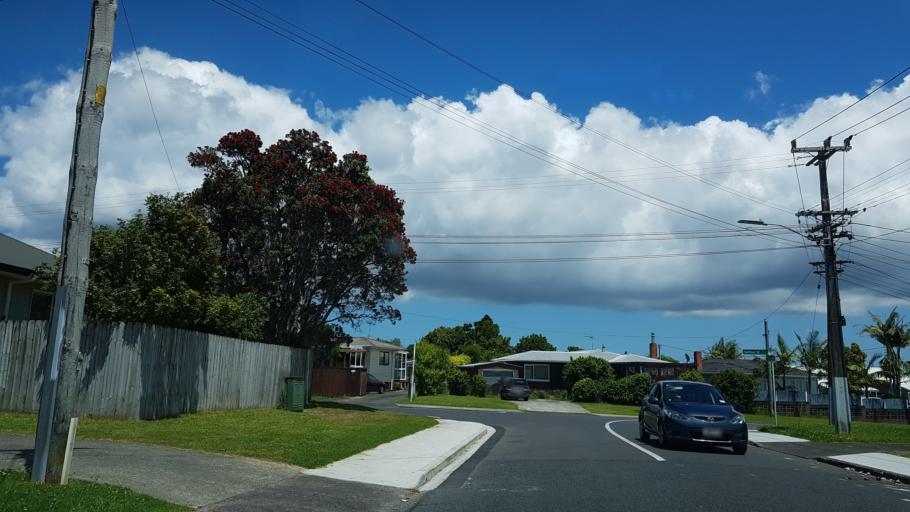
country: NZ
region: Auckland
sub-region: Auckland
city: North Shore
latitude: -36.7975
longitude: 174.6992
